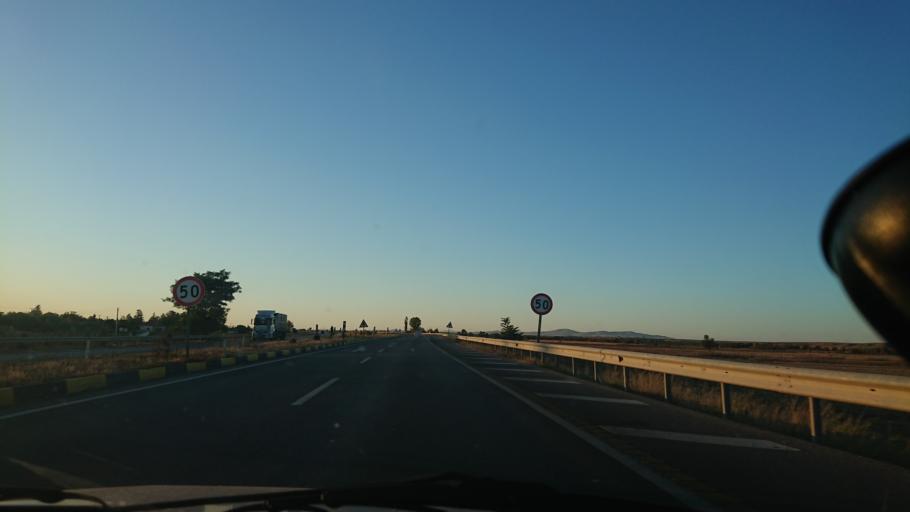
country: TR
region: Eskisehir
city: Mahmudiye
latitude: 39.5366
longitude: 30.9442
